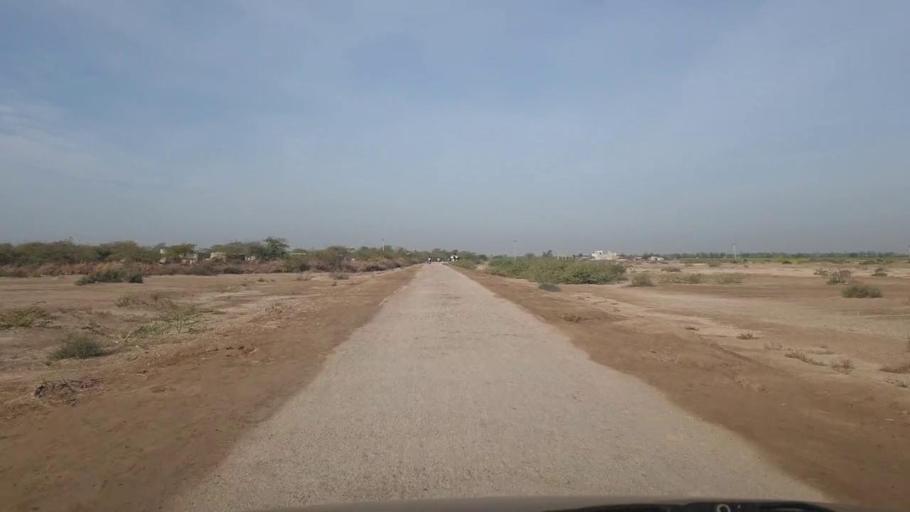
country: PK
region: Sindh
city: Umarkot
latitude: 25.3263
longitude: 69.7080
